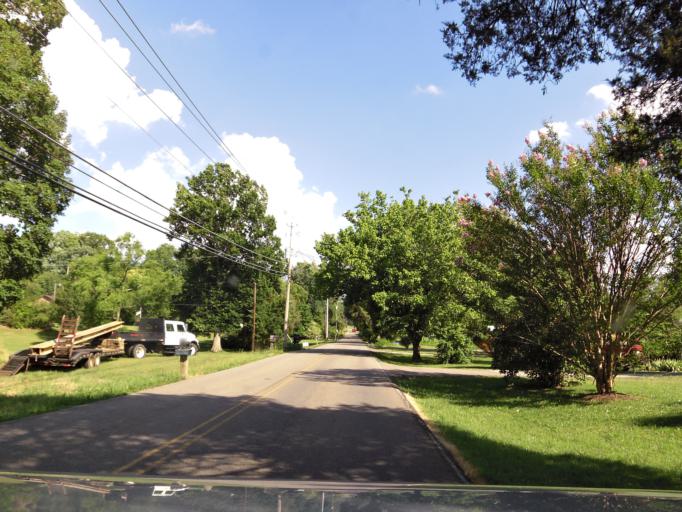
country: US
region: Tennessee
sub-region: Knox County
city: Knoxville
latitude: 36.0937
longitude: -83.9078
